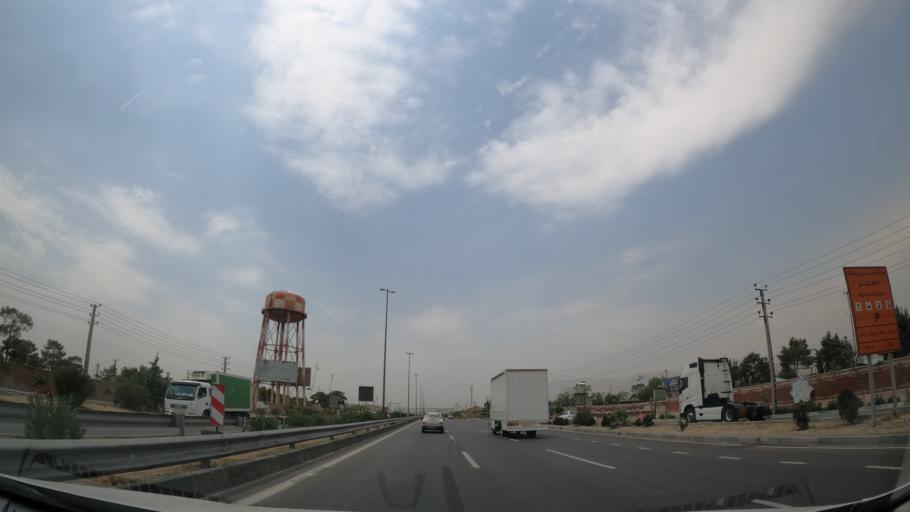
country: IR
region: Tehran
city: Shahr-e Qods
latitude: 35.6940
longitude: 51.2071
